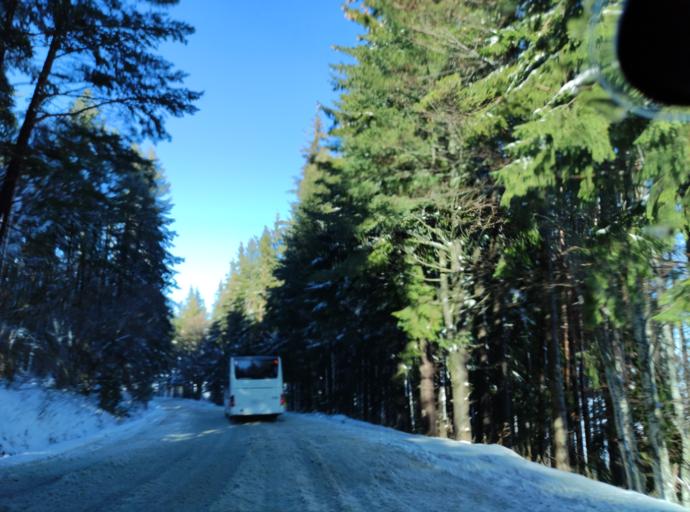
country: BG
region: Sofia-Capital
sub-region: Stolichna Obshtina
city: Sofia
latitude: 42.5928
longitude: 23.3124
